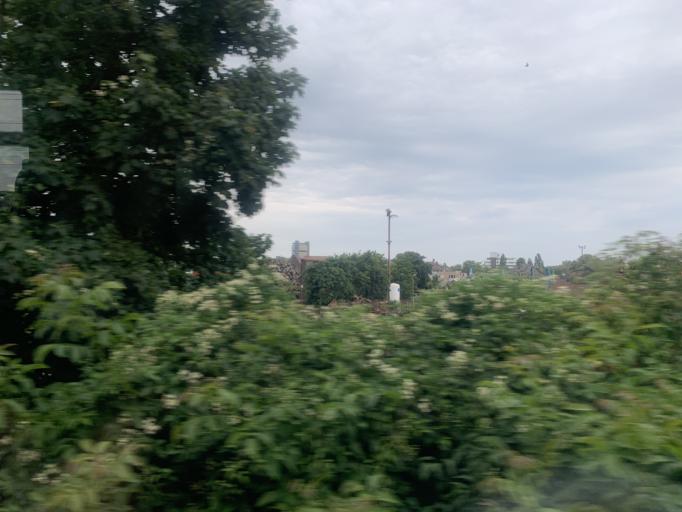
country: DE
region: North Rhine-Westphalia
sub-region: Regierungsbezirk Koln
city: Bilderstoeckchen
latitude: 50.9499
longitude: 6.9028
